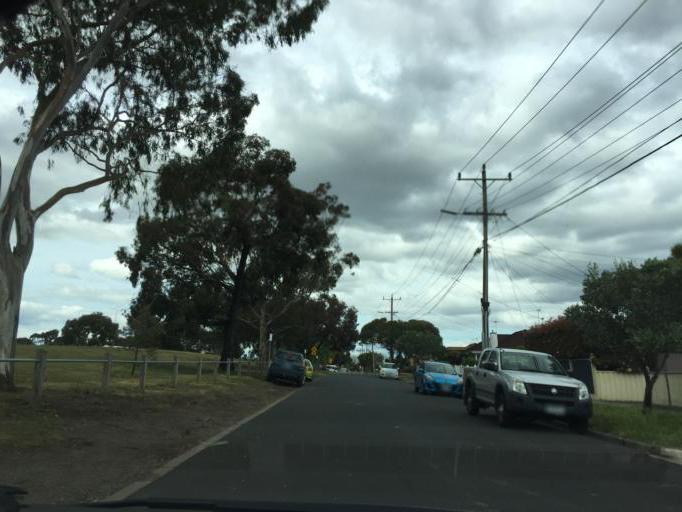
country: AU
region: Victoria
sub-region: Maribyrnong
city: Kingsville
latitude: -37.8056
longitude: 144.8713
